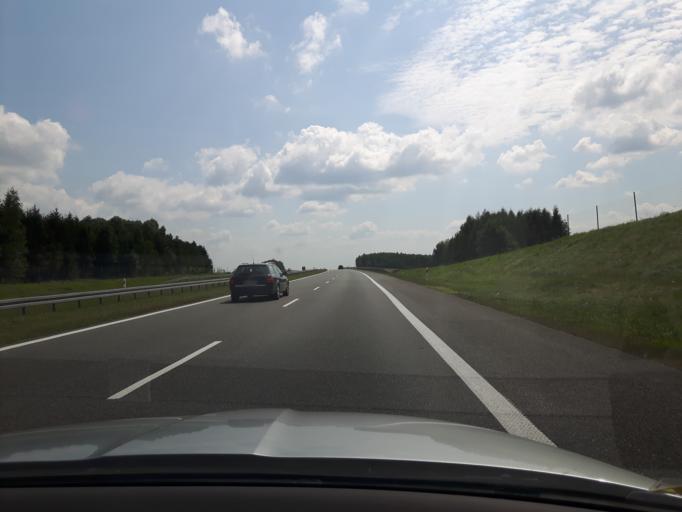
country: PL
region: Warmian-Masurian Voivodeship
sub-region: Powiat ostrodzki
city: Maldyty
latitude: 53.8400
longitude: 19.7580
